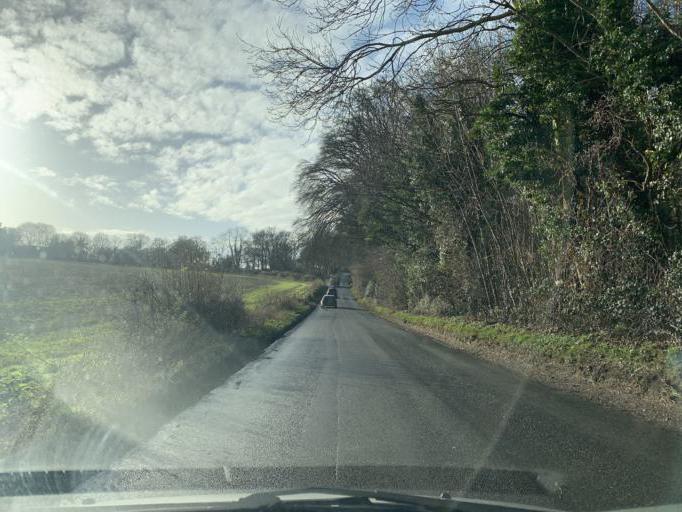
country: GB
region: England
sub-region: Wiltshire
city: Wilton
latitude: 51.0595
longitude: -1.8613
